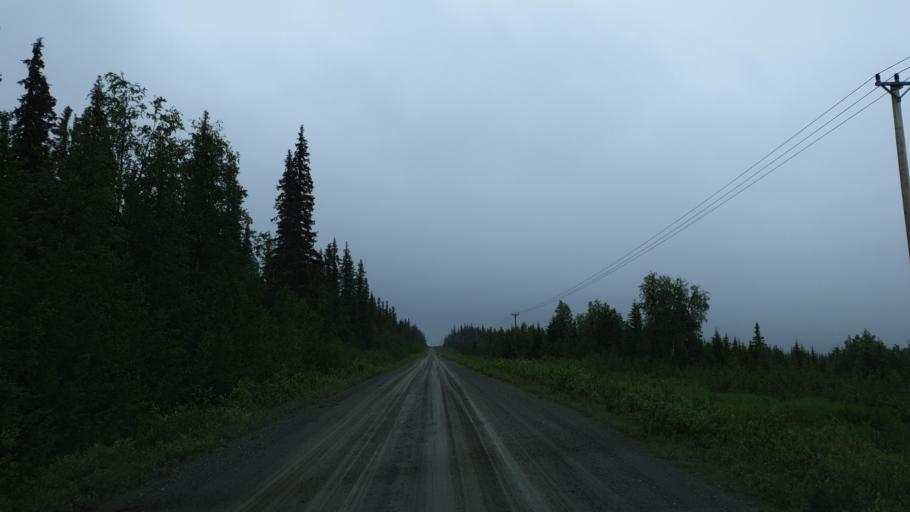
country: SE
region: Vaesterbotten
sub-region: Vilhelmina Kommun
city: Sjoberg
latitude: 65.3216
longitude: 15.9369
